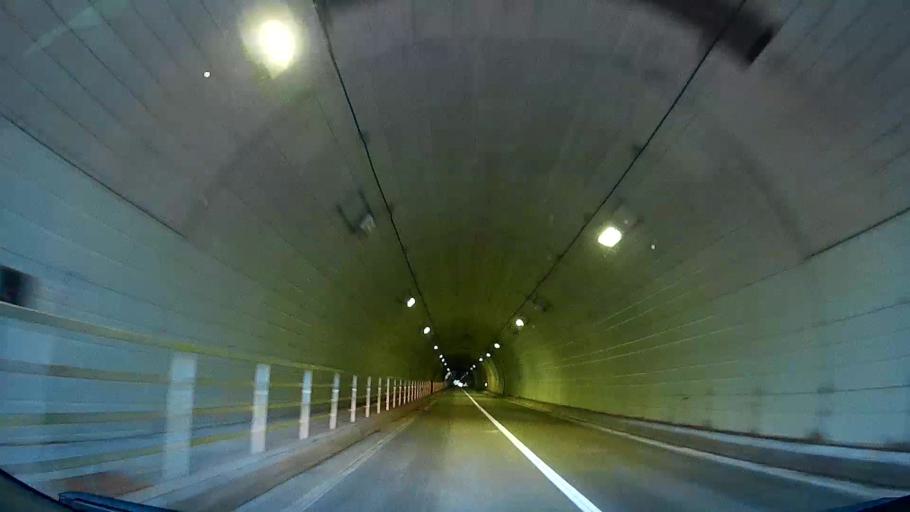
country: JP
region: Hokkaido
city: Sapporo
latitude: 42.9778
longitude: 141.1454
